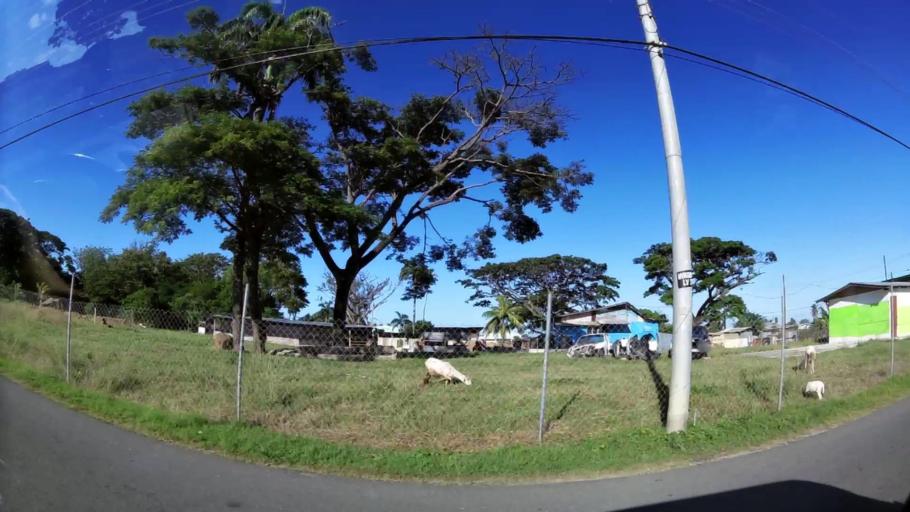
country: TT
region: Tobago
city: Scarborough
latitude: 11.1558
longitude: -60.8135
